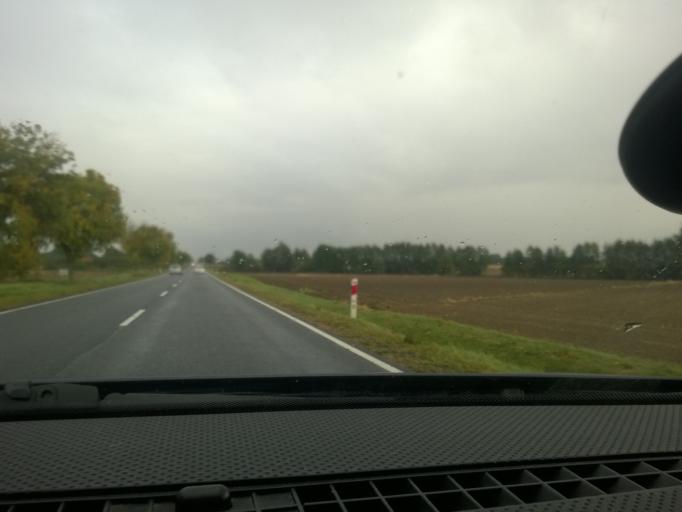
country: PL
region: Lodz Voivodeship
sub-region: Powiat sieradzki
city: Blaszki
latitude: 51.6781
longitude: 18.3506
